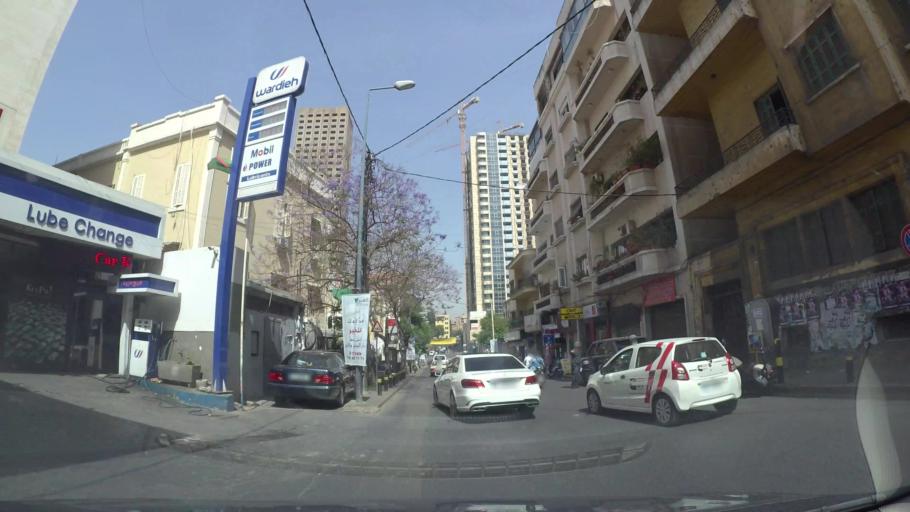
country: LB
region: Beyrouth
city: Beirut
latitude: 33.8947
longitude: 35.4947
